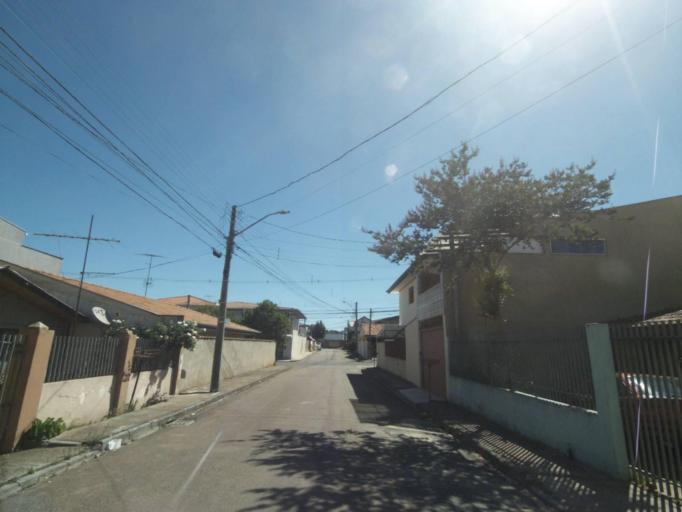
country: BR
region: Parana
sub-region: Curitiba
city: Curitiba
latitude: -25.4618
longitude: -49.3511
